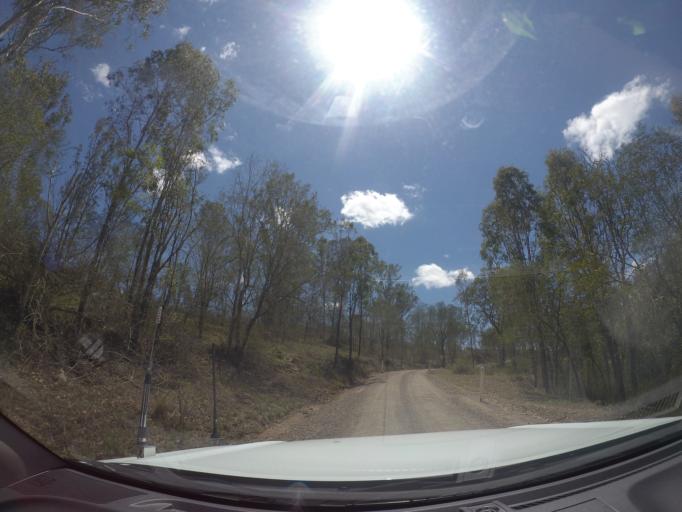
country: AU
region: Queensland
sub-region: Logan
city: Cedar Vale
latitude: -27.8597
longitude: 152.8547
